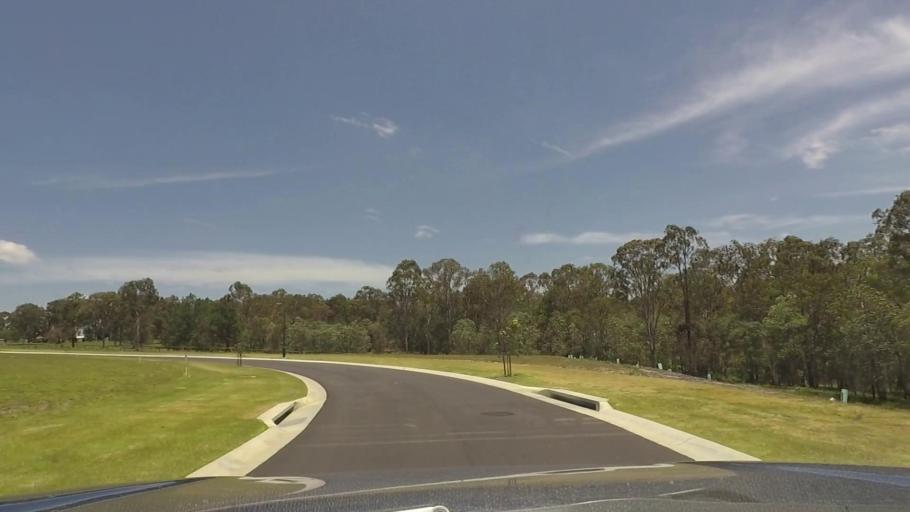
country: AU
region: Queensland
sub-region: Logan
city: Chambers Flat
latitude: -27.7730
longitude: 153.0871
